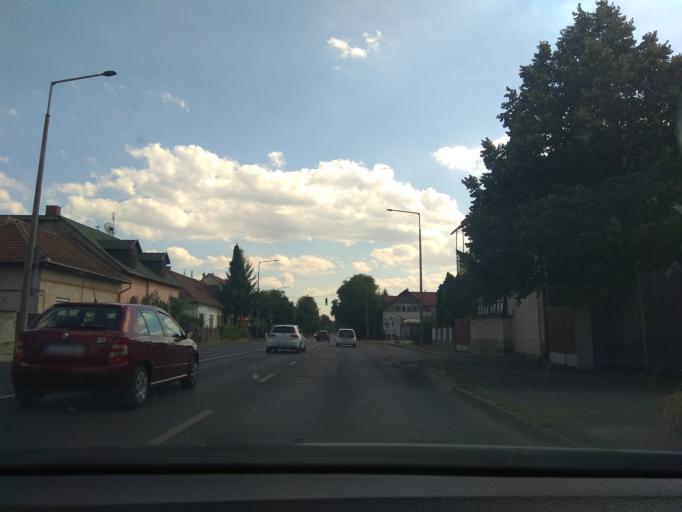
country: HU
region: Borsod-Abauj-Zemplen
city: Miskolc
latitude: 48.0935
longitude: 20.7923
